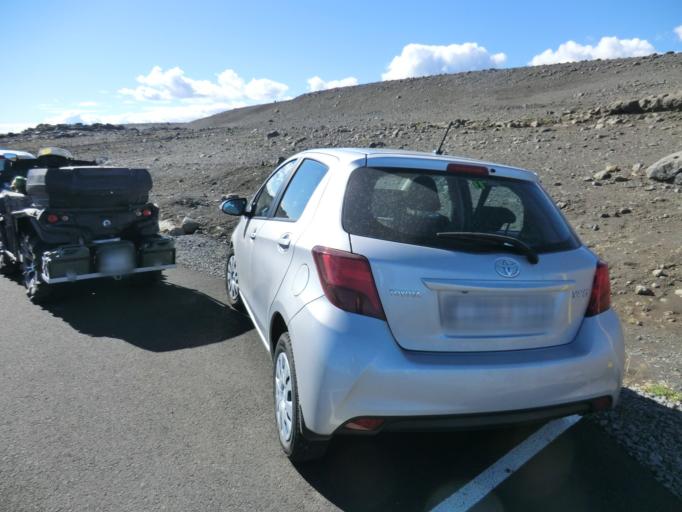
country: IS
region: Northeast
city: Husavik
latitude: 65.8133
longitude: -16.4013
